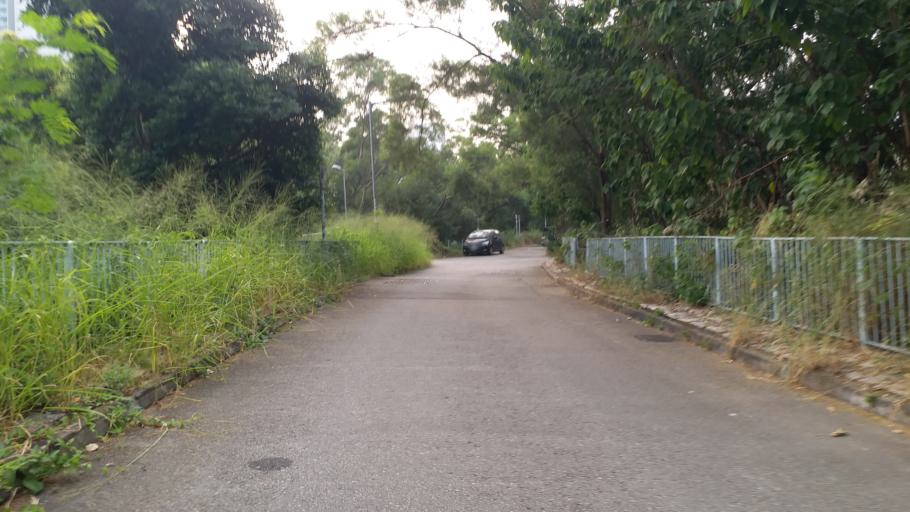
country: HK
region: Yuen Long
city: Yuen Long Kau Hui
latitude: 22.4545
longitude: 114.0102
